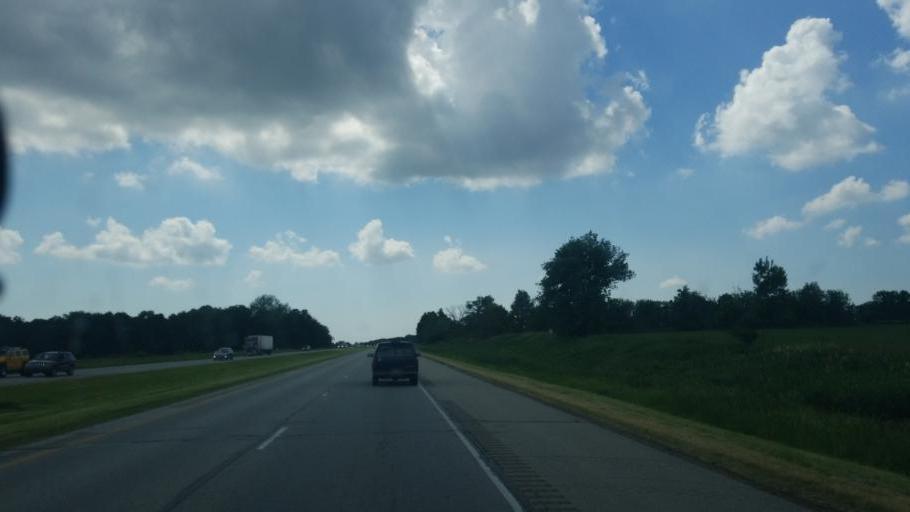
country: US
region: Indiana
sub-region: Kosciusko County
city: Warsaw
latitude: 41.2692
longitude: -85.9309
